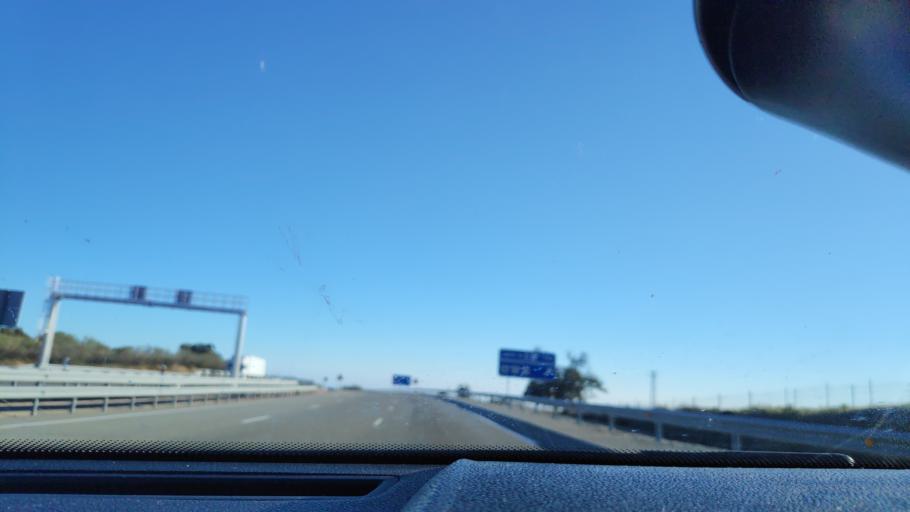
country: ES
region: Andalusia
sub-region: Provincia de Sevilla
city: El Ronquillo
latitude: 37.6381
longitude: -6.1543
